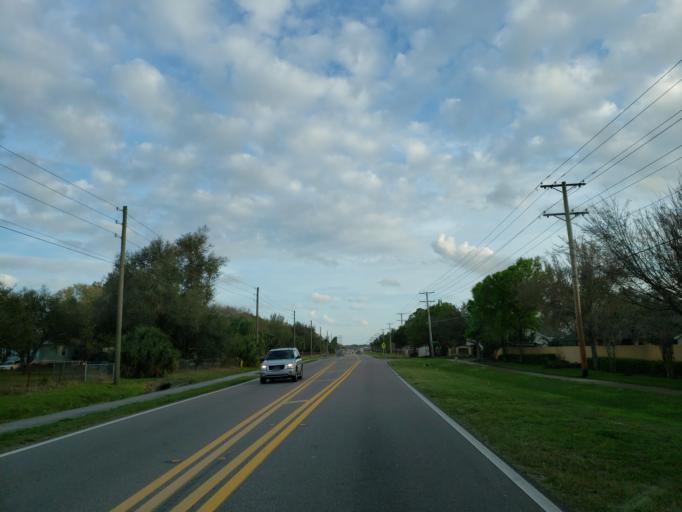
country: US
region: Florida
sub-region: Hillsborough County
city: Balm
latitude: 27.8054
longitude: -82.2893
